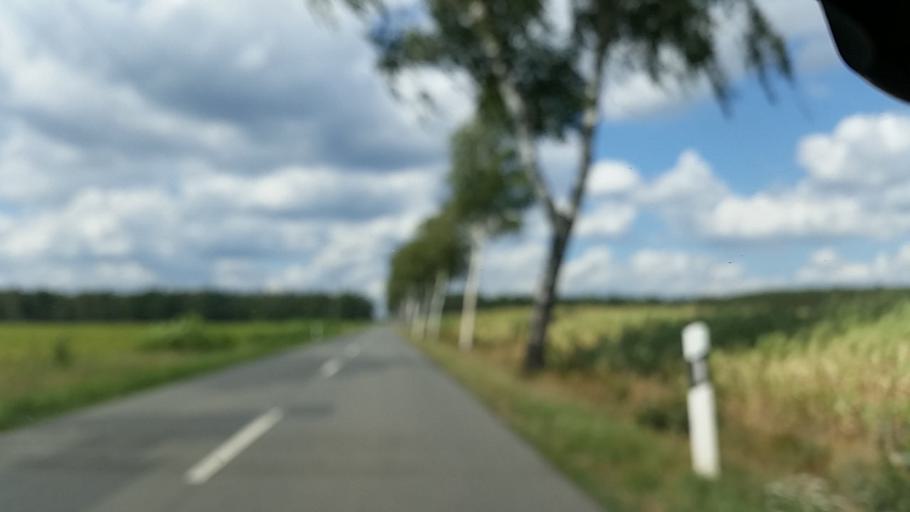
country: DE
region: Lower Saxony
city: Dedelstorf
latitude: 52.7207
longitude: 10.5223
